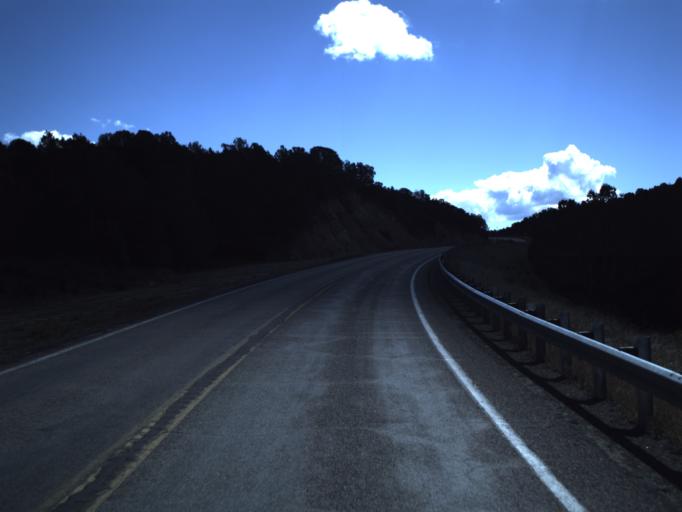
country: US
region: Utah
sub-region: Washington County
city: Enterprise
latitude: 37.5390
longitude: -113.6562
